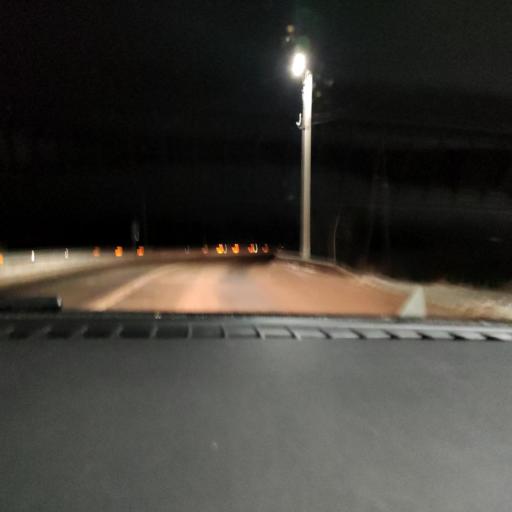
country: RU
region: Samara
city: Osinki
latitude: 52.8961
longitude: 49.5063
